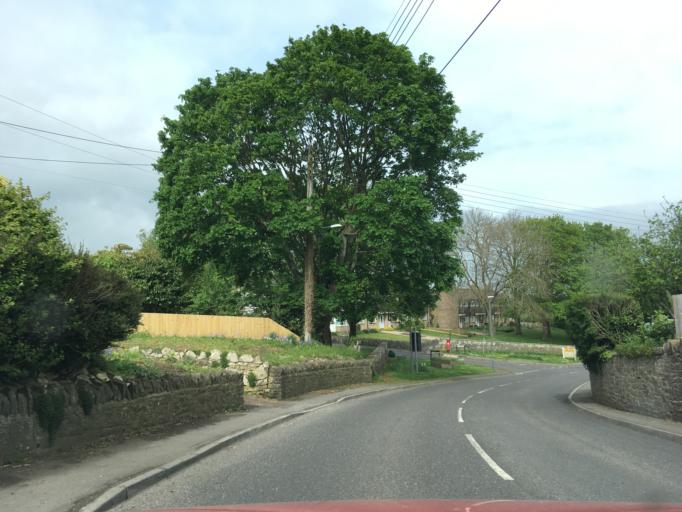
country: GB
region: England
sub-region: Bath and North East Somerset
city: Paulton
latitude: 51.3078
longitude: -2.5092
